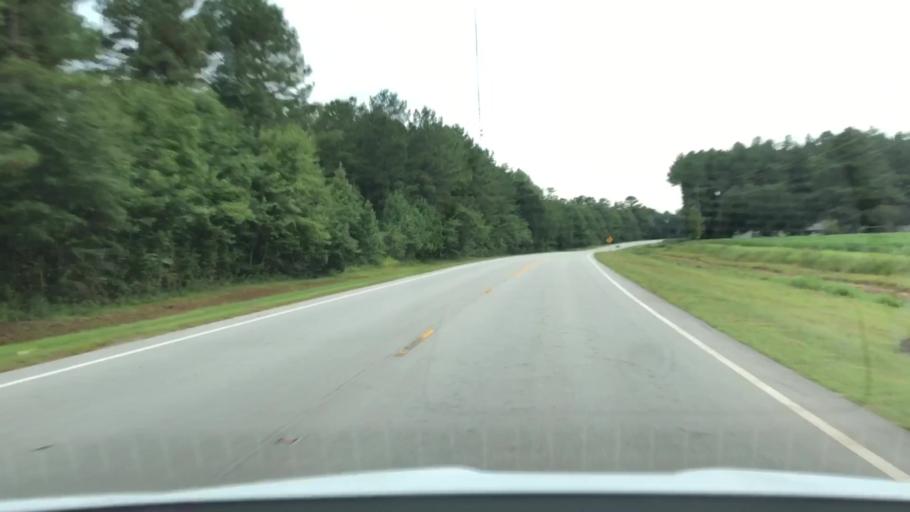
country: US
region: North Carolina
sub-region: Jones County
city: Trenton
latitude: 35.0380
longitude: -77.3461
